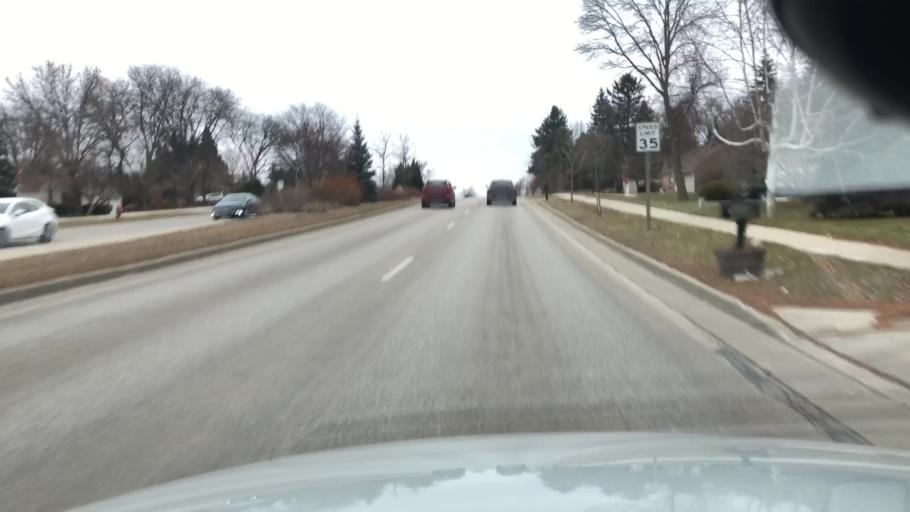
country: US
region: Wisconsin
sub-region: Waukesha County
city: Brookfield
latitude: 43.0522
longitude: -88.1265
